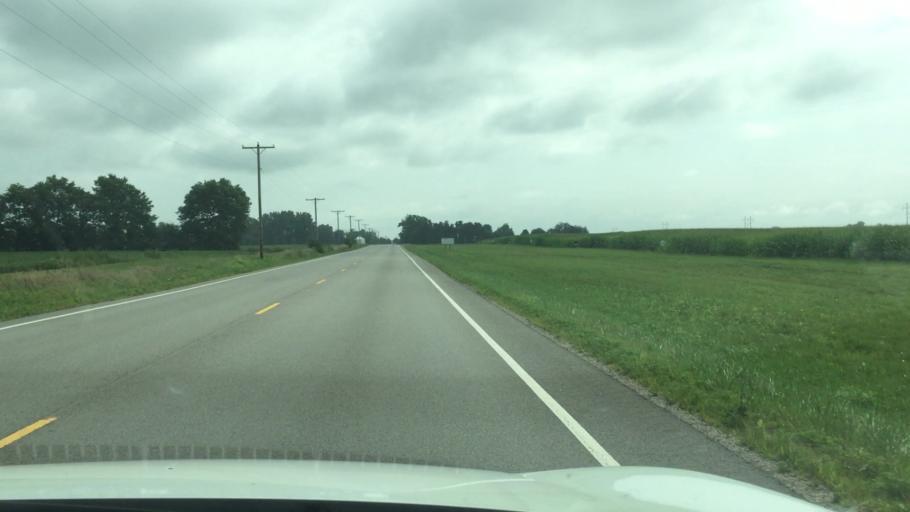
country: US
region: Ohio
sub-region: Union County
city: Marysville
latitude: 40.1637
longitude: -83.4481
